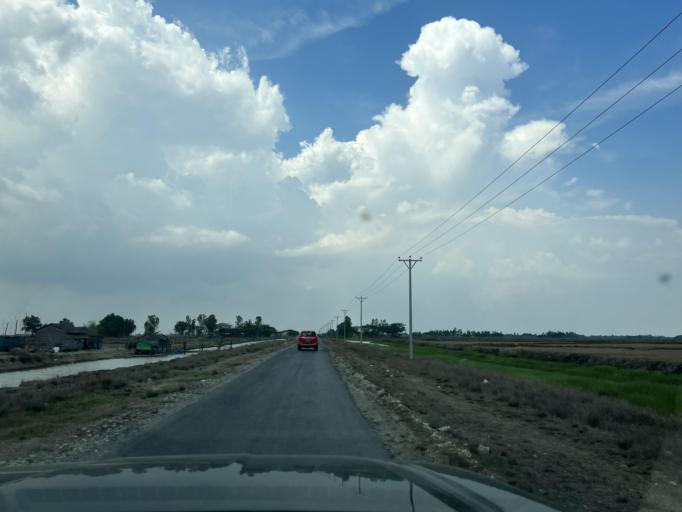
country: MM
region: Ayeyarwady
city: Pyapon
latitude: 16.0258
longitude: 95.6079
